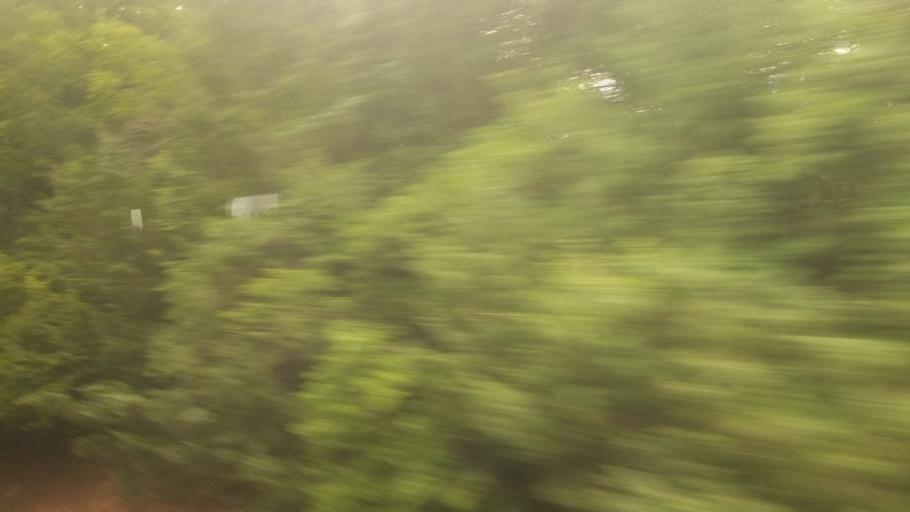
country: US
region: Kansas
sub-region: Shawnee County
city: Topeka
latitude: 39.0234
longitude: -95.6757
